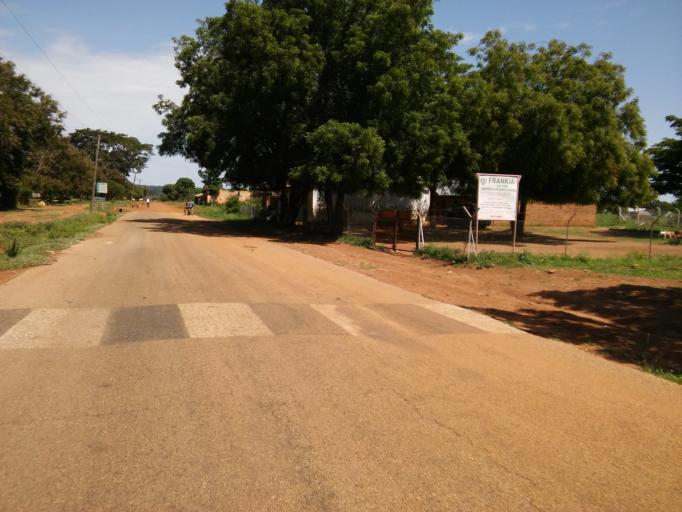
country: UG
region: Eastern Region
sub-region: Kumi District
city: Kumi
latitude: 1.4862
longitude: 33.9242
